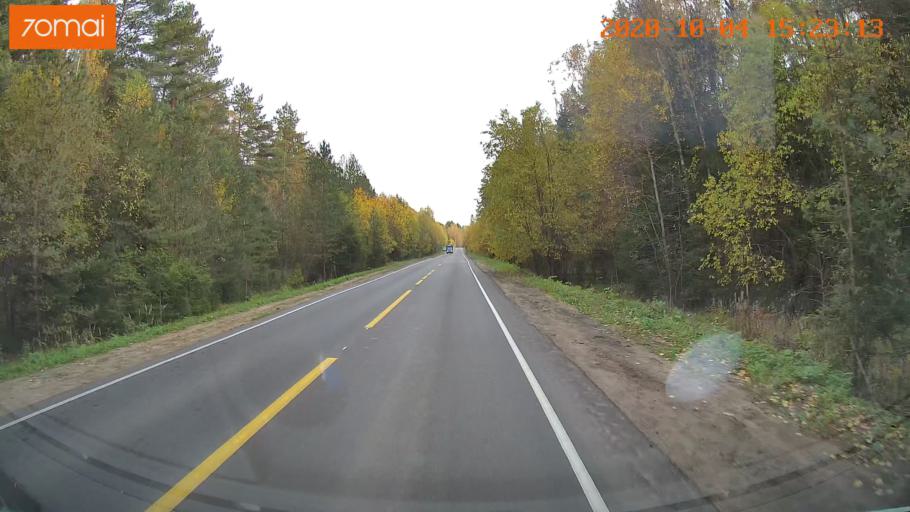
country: RU
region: Ivanovo
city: Bogorodskoye
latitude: 57.0757
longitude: 40.9467
